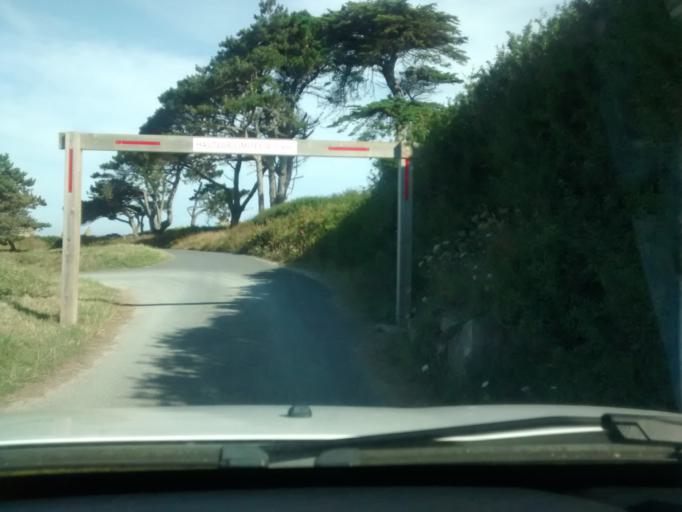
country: FR
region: Brittany
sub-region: Departement des Cotes-d'Armor
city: Plougrescant
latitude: 48.8662
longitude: -3.2306
